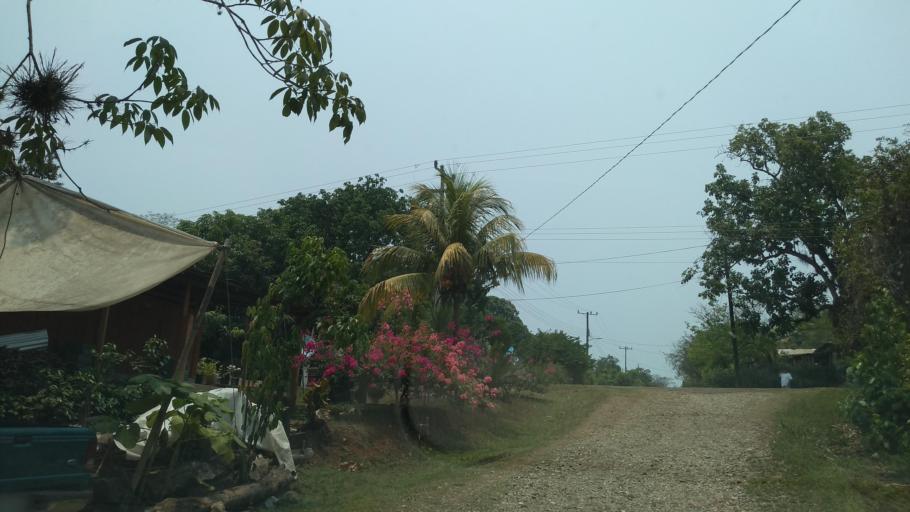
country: MX
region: Veracruz
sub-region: Tezonapa
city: Laguna Chica (Pueblo Nuevo)
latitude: 18.5128
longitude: -96.7618
